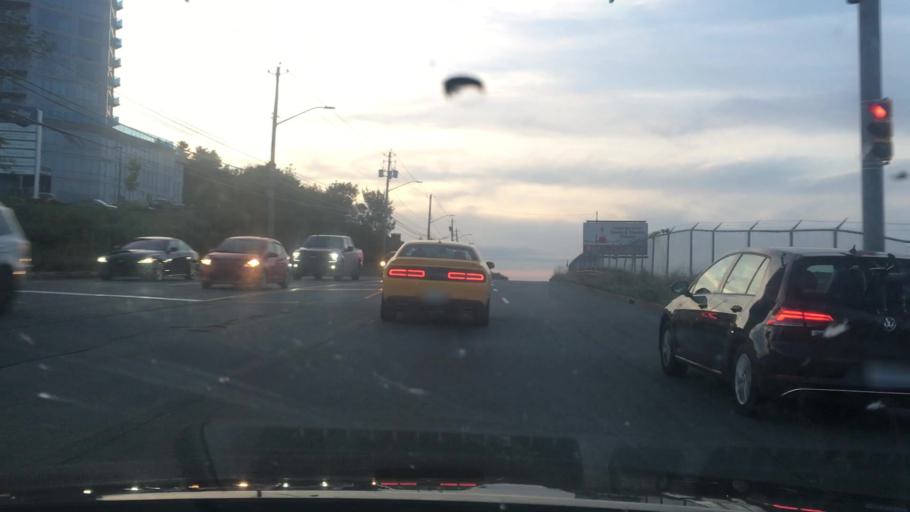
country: CA
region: Nova Scotia
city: Dartmouth
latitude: 44.6643
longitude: -63.6343
